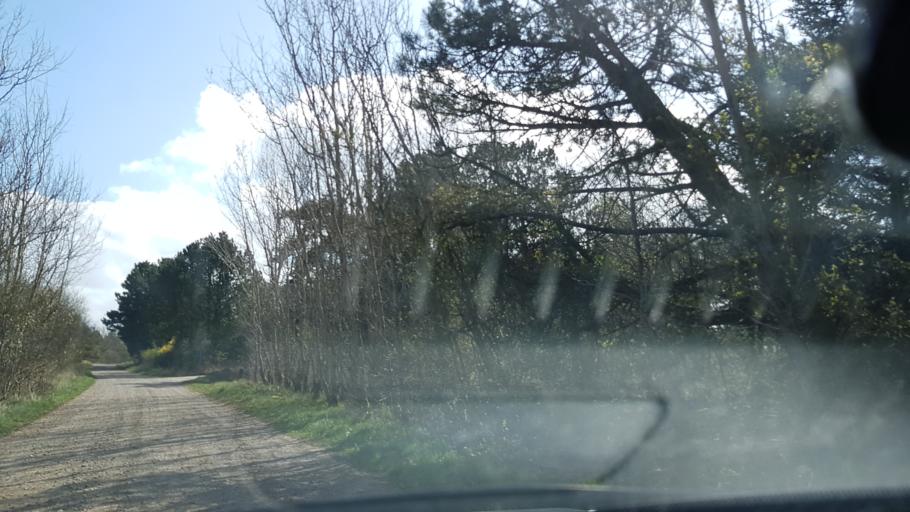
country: DE
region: Schleswig-Holstein
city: List
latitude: 55.0846
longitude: 8.5386
